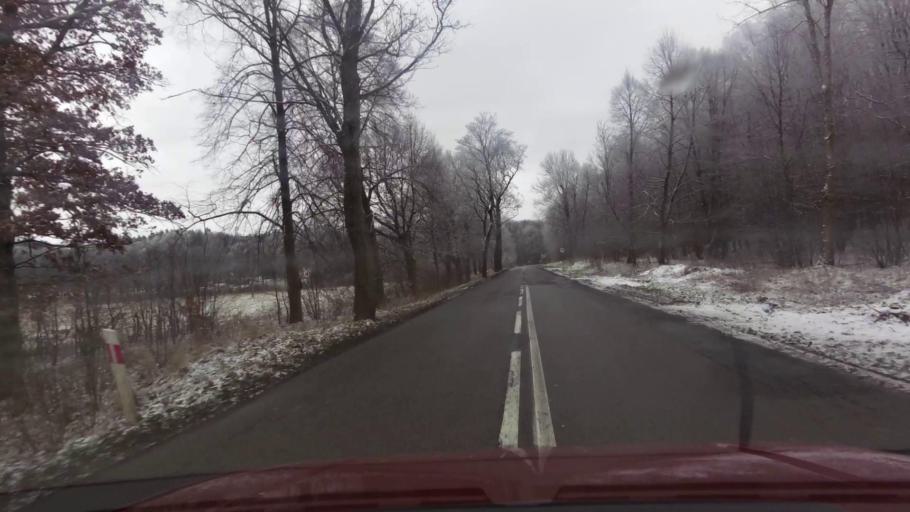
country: PL
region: West Pomeranian Voivodeship
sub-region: Powiat swidwinski
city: Polczyn-Zdroj
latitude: 53.7948
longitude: 16.0531
